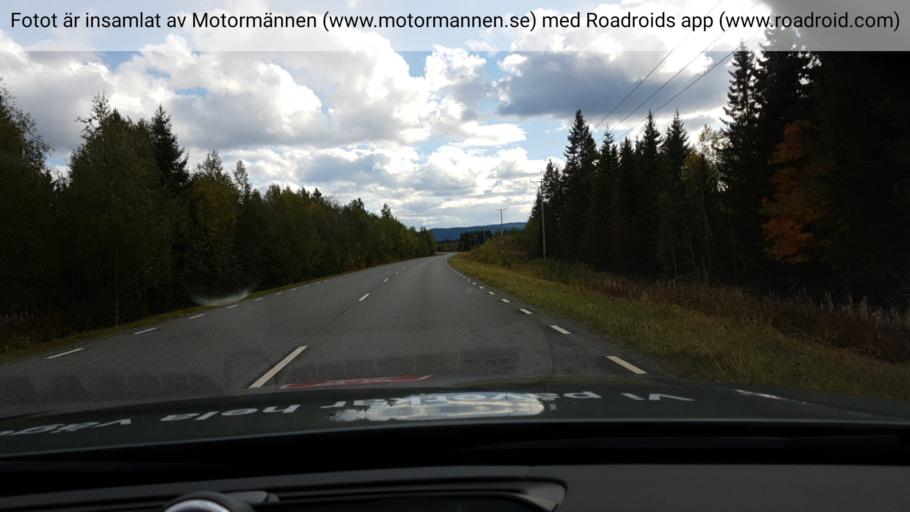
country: SE
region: Jaemtland
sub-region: Are Kommun
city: Jarpen
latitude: 63.3761
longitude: 13.4290
